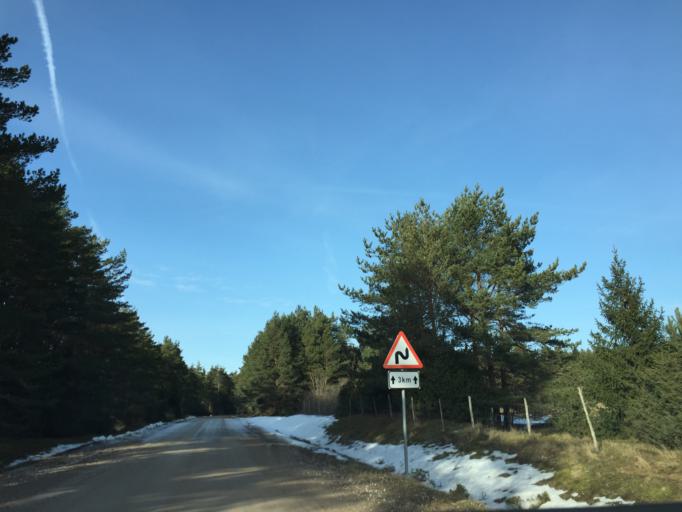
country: EE
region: Saare
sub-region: Kuressaare linn
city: Kuressaare
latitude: 58.3704
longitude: 22.0181
